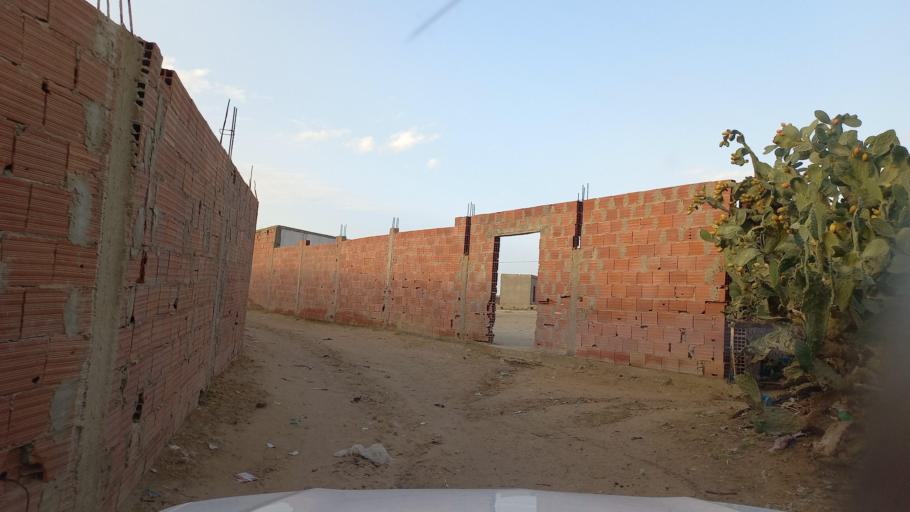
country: TN
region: Al Qasrayn
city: Kasserine
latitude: 35.2694
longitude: 9.0681
